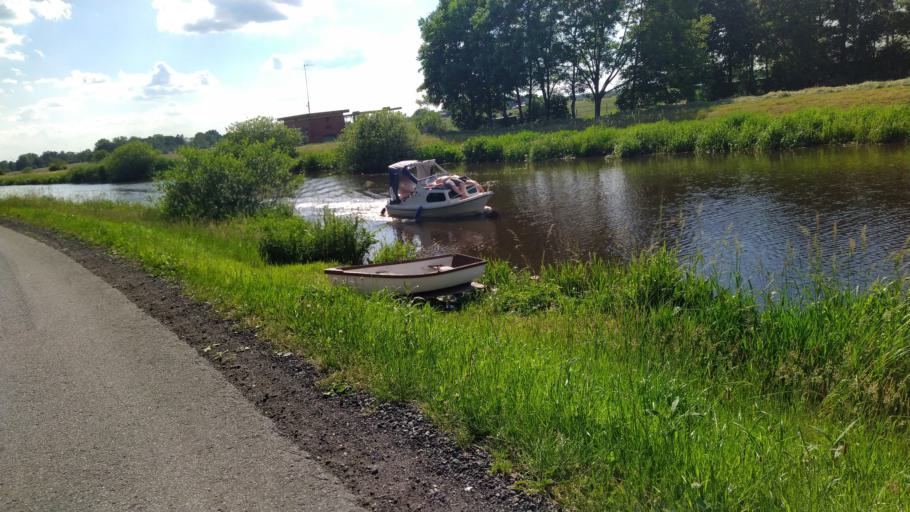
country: DE
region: Lower Saxony
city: Odisheim
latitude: 53.6682
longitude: 8.9119
